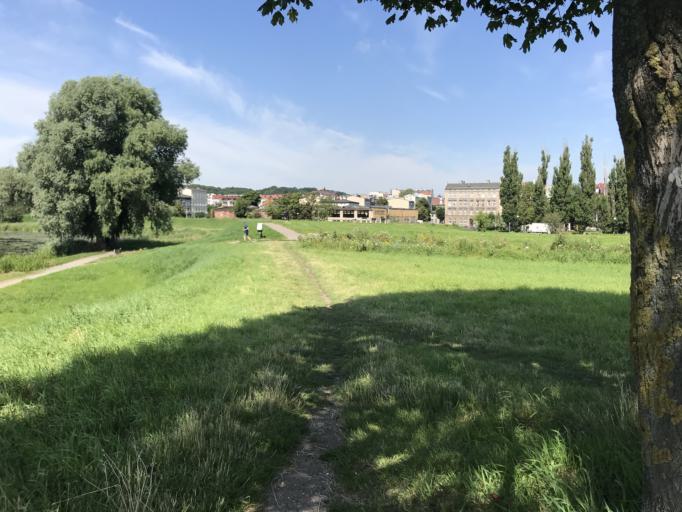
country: PL
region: Pomeranian Voivodeship
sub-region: Gdansk
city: Gdansk
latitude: 54.3384
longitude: 18.6586
